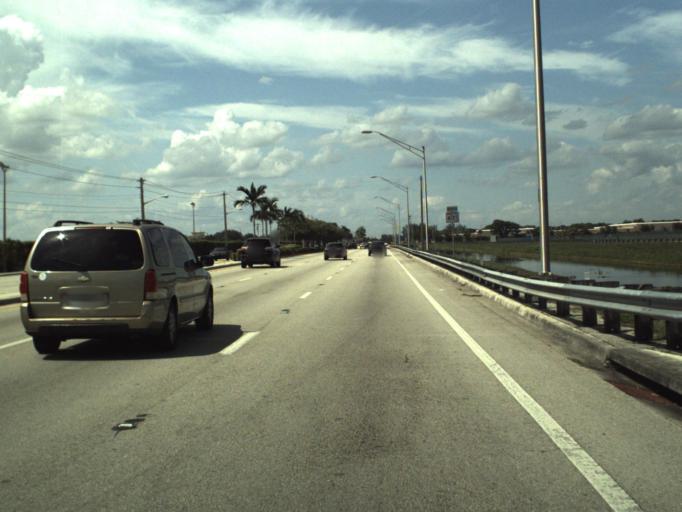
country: US
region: Florida
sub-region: Broward County
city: Miramar
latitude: 26.0017
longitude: -80.2478
